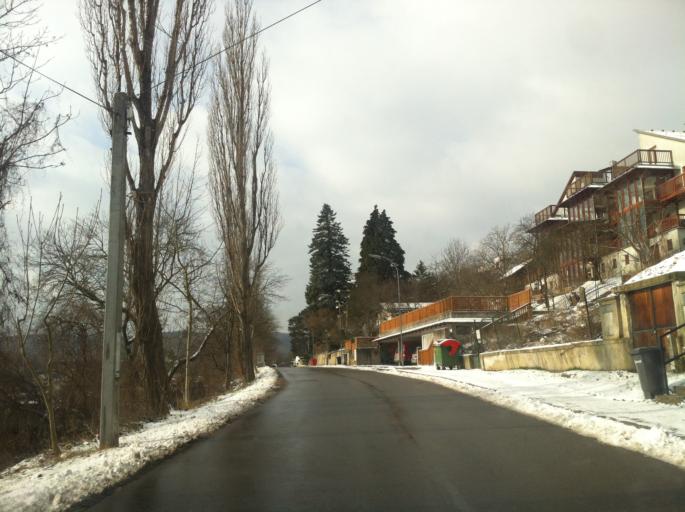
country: AT
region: Lower Austria
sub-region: Politischer Bezirk Wien-Umgebung
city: Purkersdorf
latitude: 48.2083
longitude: 16.1911
